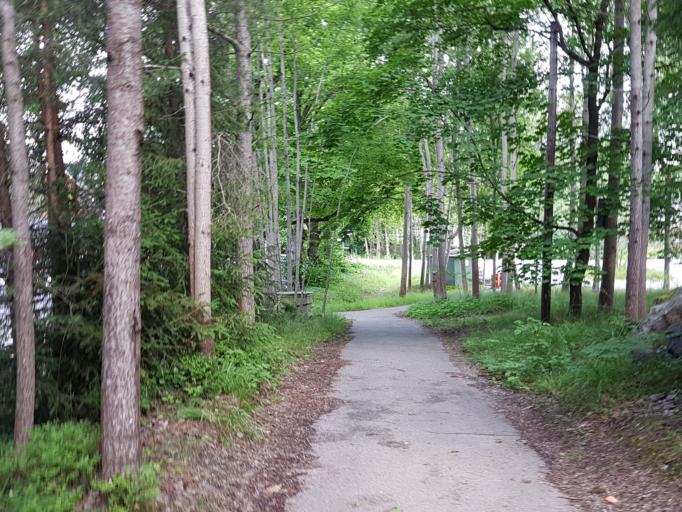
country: SE
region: Stockholm
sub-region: Nacka Kommun
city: Kummelnas
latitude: 59.3470
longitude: 18.2423
